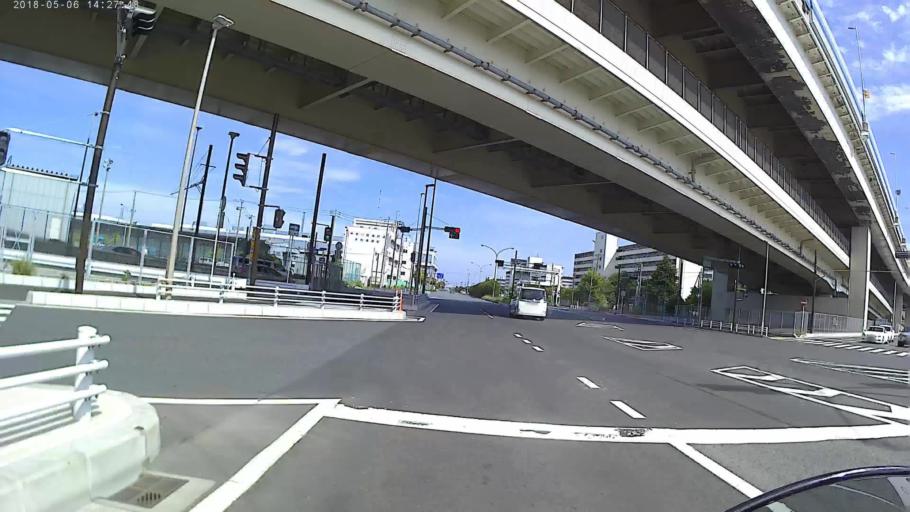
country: JP
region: Kanagawa
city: Yokohama
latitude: 35.4314
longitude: 139.6705
